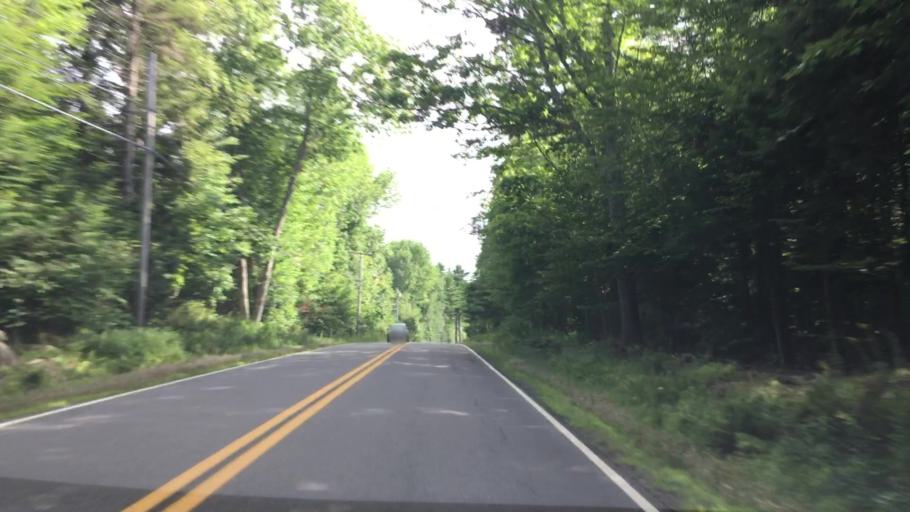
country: US
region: Maine
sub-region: Waldo County
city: Belfast
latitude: 44.3907
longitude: -69.0330
